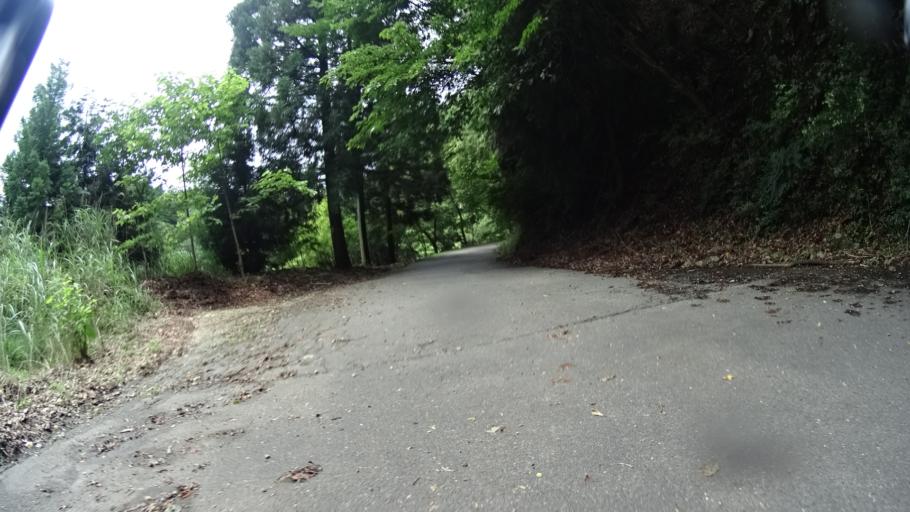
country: JP
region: Saitama
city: Chichibu
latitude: 35.8920
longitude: 139.1352
